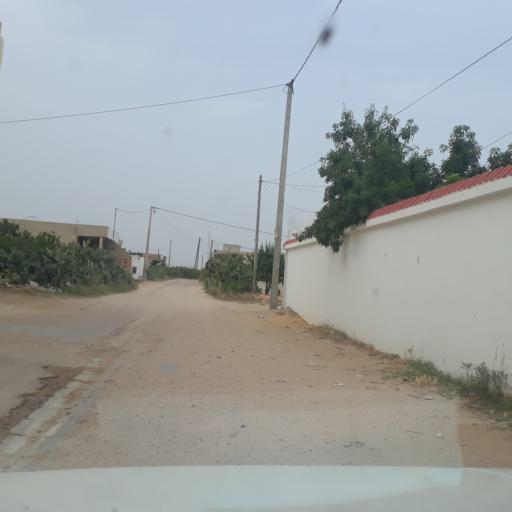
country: TN
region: Safaqis
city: Al Qarmadah
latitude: 34.8247
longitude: 10.7761
